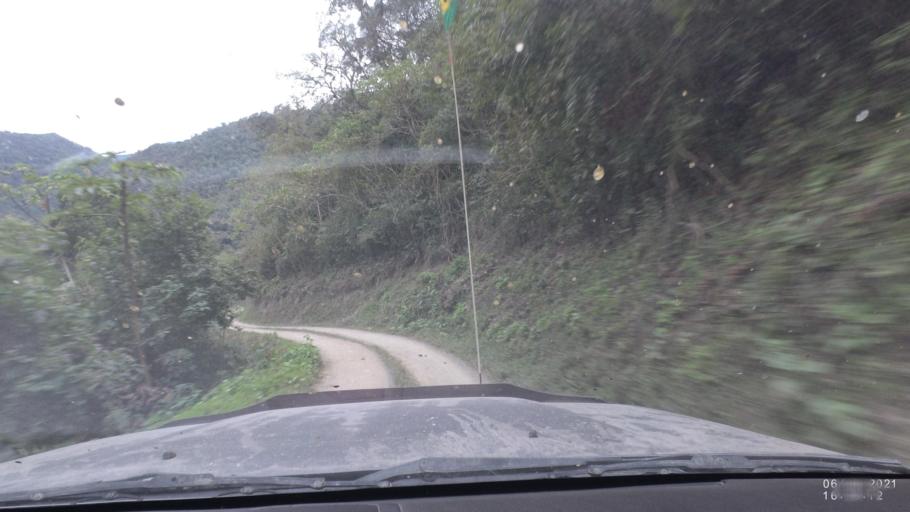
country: BO
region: La Paz
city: Quime
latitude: -16.5275
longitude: -66.7532
